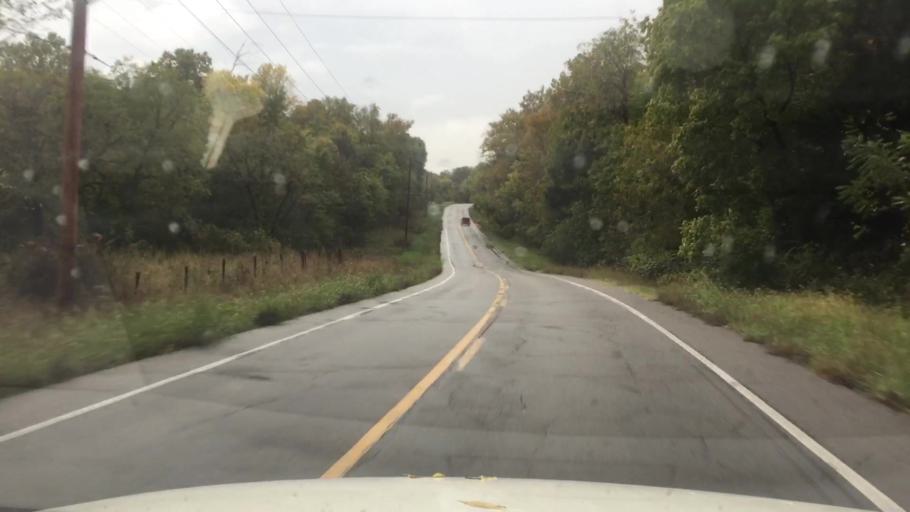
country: US
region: Missouri
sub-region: Boone County
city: Columbia
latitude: 38.8843
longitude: -92.4281
